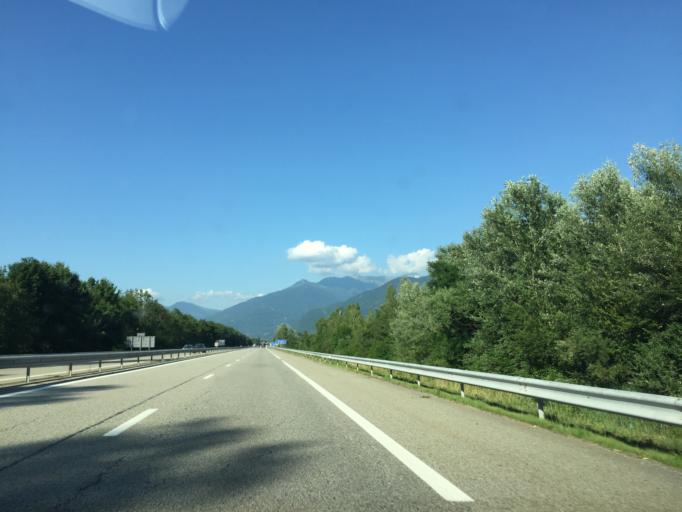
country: FR
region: Rhone-Alpes
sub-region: Departement de la Savoie
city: Sainte-Helene-sur-Isere
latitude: 45.6131
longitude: 6.2974
